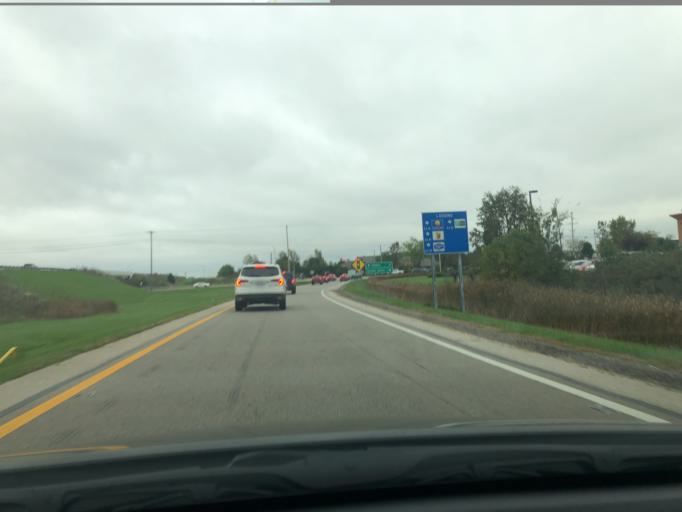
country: US
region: Ohio
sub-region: Union County
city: Marysville
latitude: 40.2403
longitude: -83.3475
